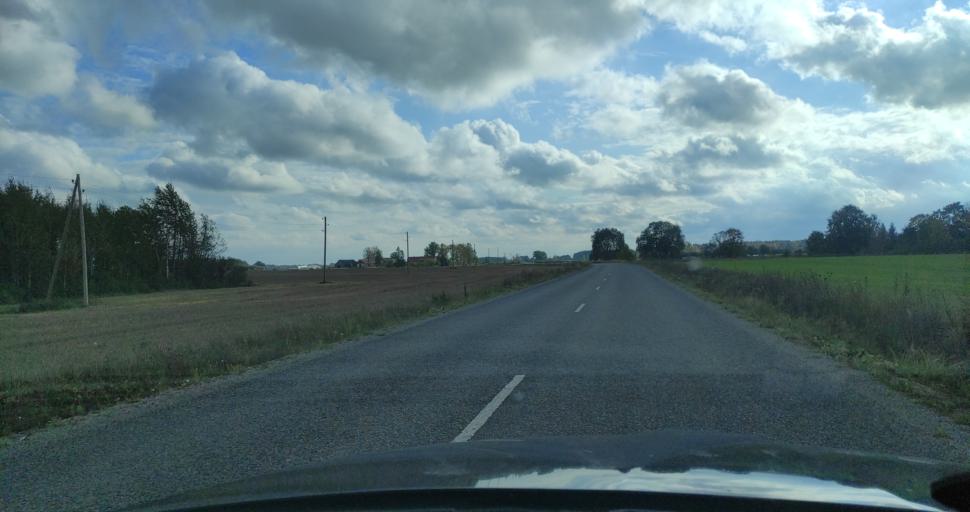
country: LV
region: Talsu Rajons
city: Sabile
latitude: 56.9268
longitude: 22.3949
